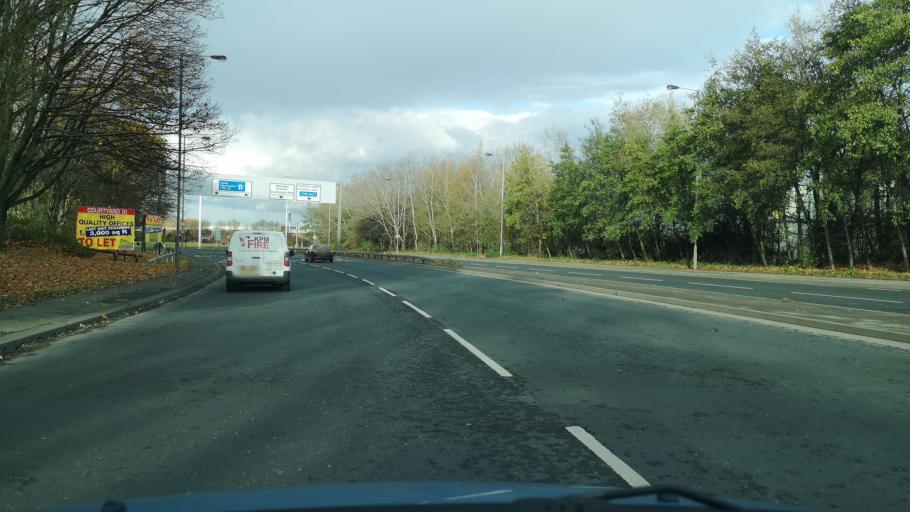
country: GB
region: England
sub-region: City and Borough of Wakefield
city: Normanton
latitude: 53.7061
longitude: -1.3969
